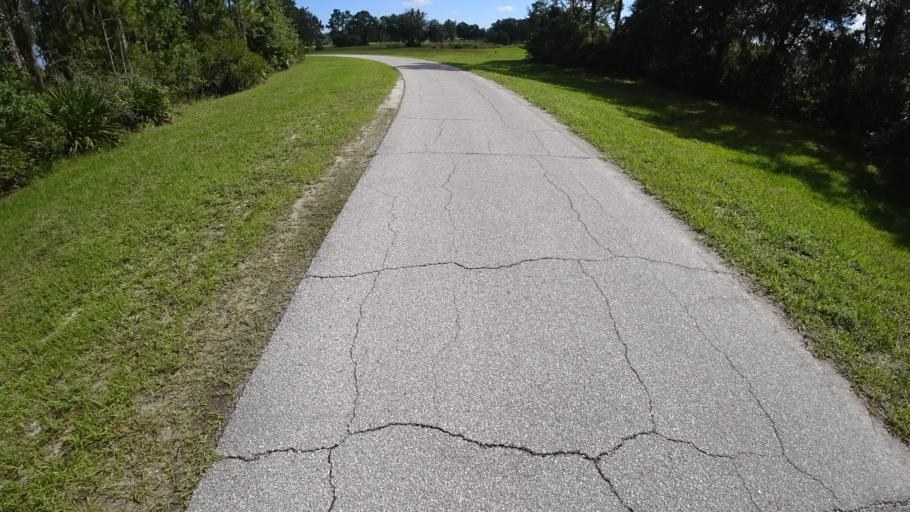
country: US
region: Florida
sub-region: Sarasota County
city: The Meadows
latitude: 27.3968
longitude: -82.3242
